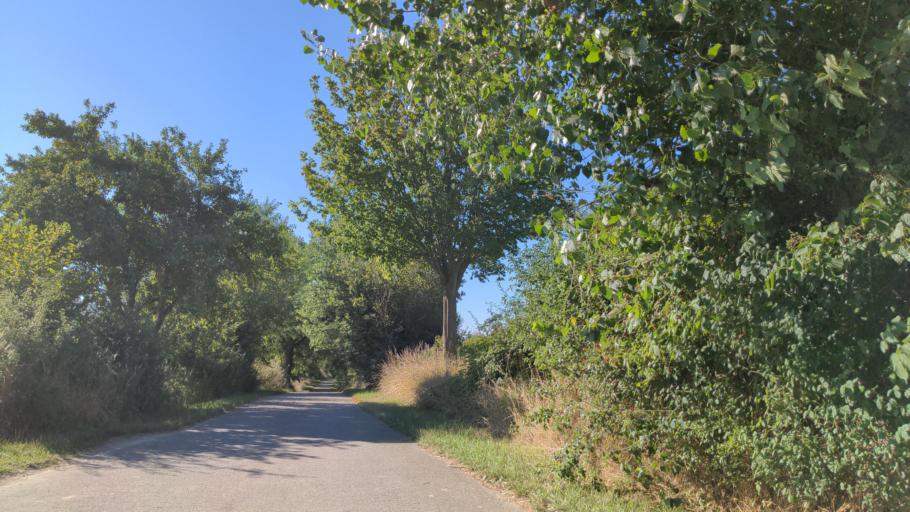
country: DE
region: Mecklenburg-Vorpommern
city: Ostseebad Boltenhagen
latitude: 54.0067
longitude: 11.1865
